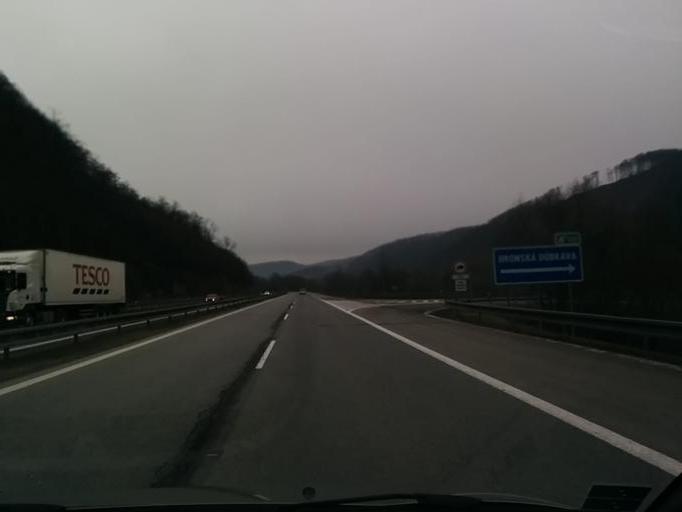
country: SK
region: Banskobystricky
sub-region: Okres Banska Bystrica
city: Zvolen
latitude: 48.5631
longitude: 19.0186
